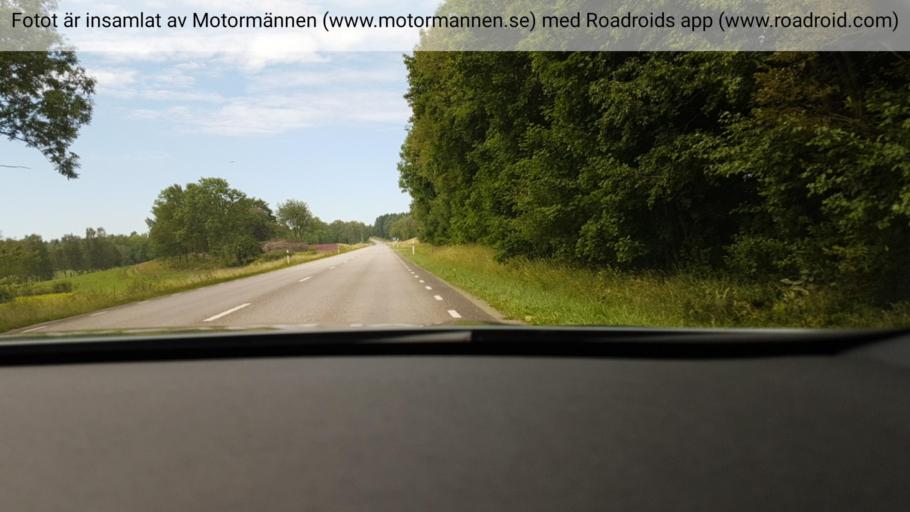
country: SE
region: Vaestra Goetaland
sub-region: Falkopings Kommun
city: Akarp
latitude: 58.2181
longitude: 13.6385
